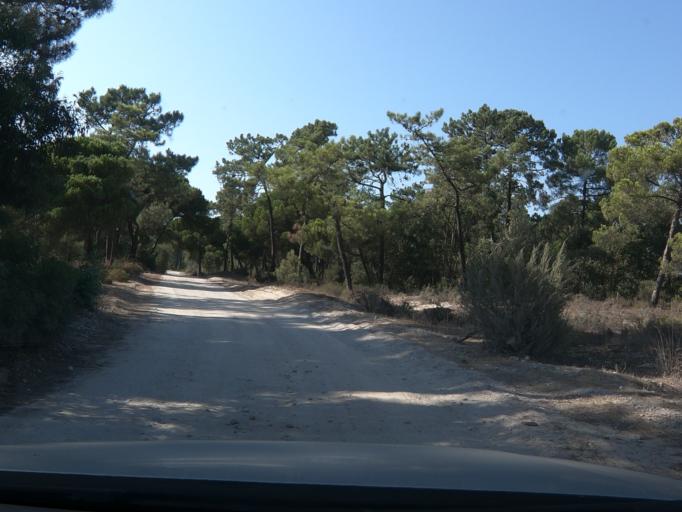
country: PT
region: Setubal
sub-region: Setubal
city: Setubal
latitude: 38.4681
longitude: -8.8734
